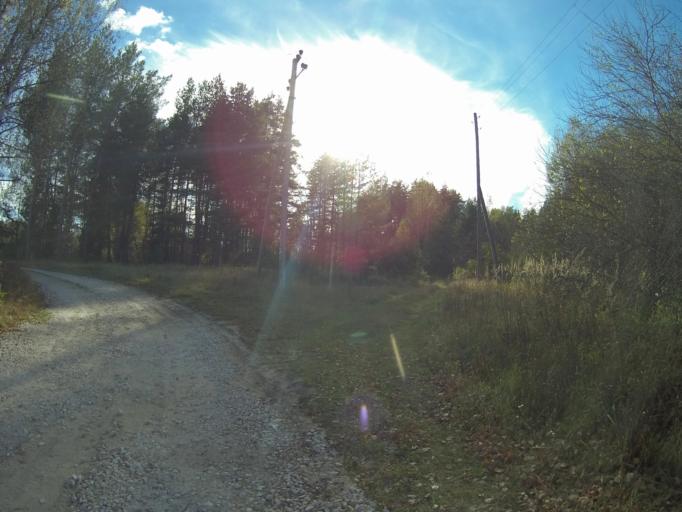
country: RU
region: Vladimir
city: Golovino
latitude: 55.9893
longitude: 40.5214
